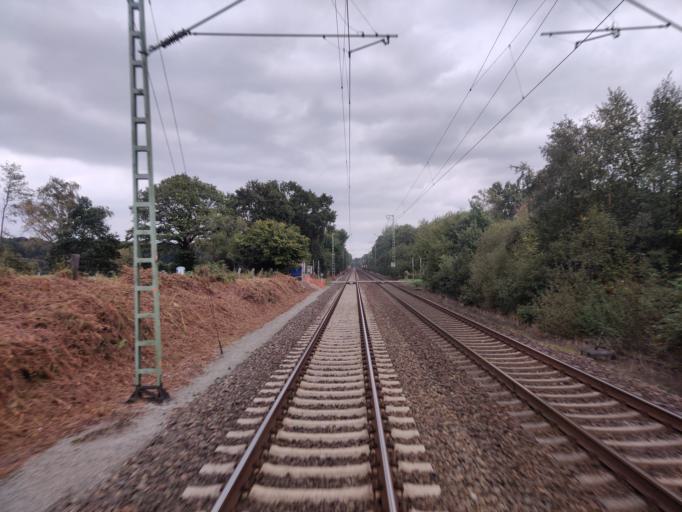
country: DE
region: Lower Saxony
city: Osterholz-Scharmbeck
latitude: 53.2031
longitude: 8.7736
